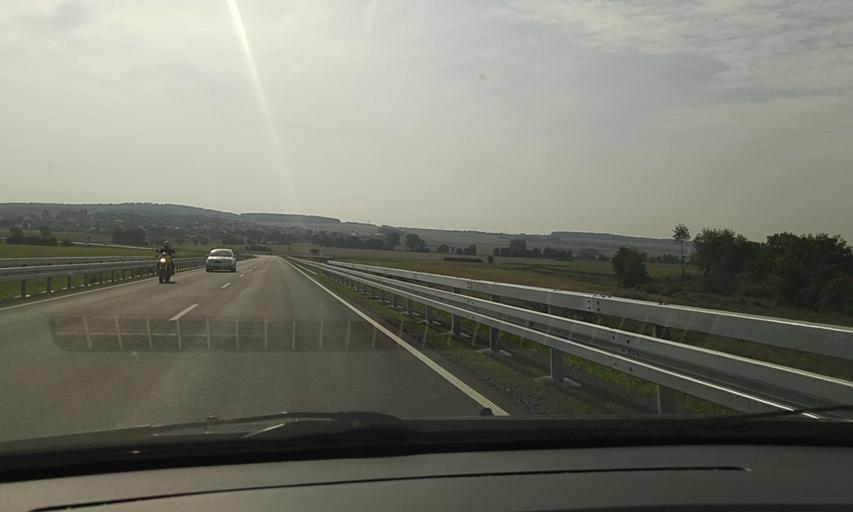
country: DE
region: Hesse
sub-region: Regierungsbezirk Darmstadt
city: Friedberg
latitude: 50.2879
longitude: 8.7794
